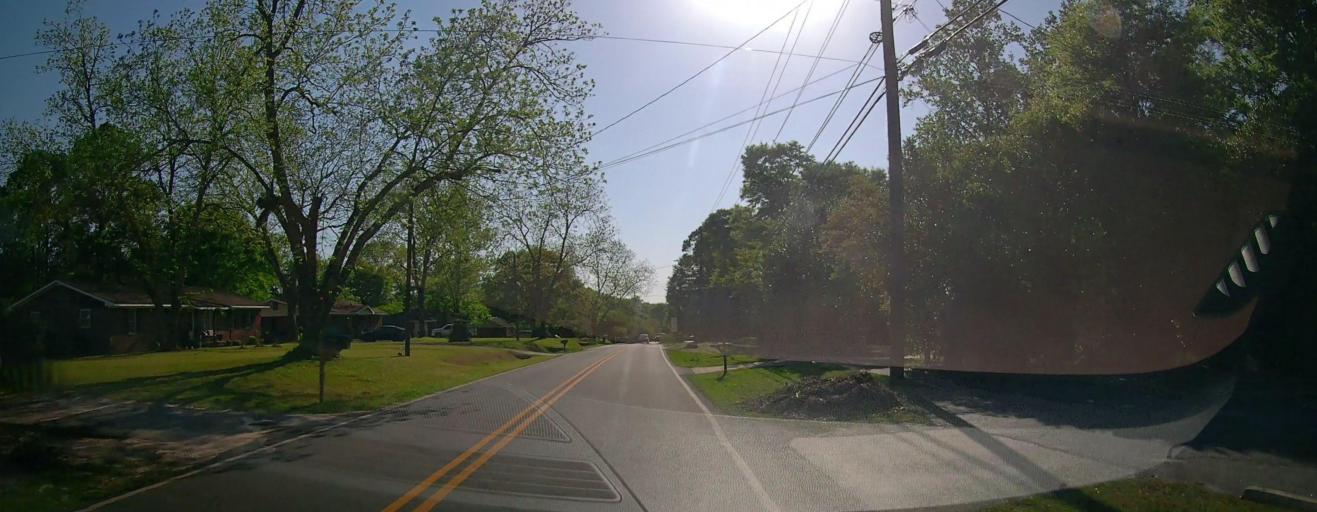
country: US
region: Georgia
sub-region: Houston County
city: Perry
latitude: 32.4497
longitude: -83.7234
